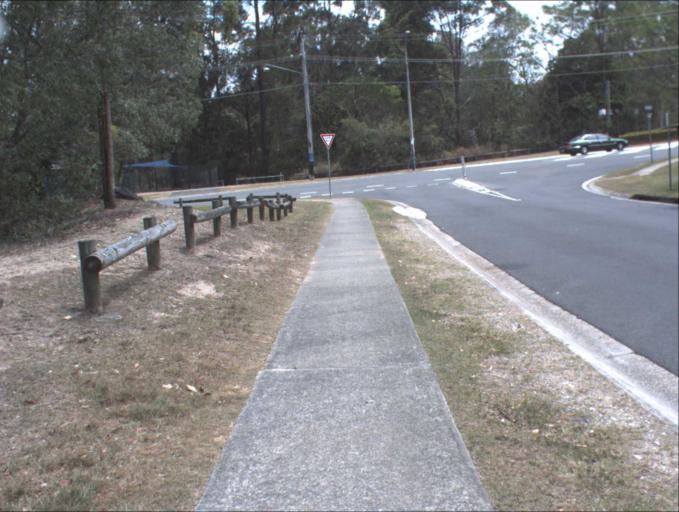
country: AU
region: Queensland
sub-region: Logan
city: Slacks Creek
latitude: -27.6447
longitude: 153.1762
